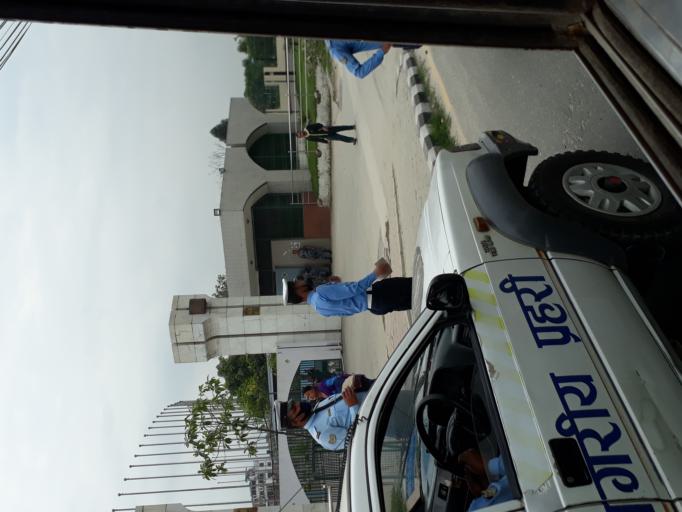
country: NP
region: Central Region
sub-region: Bagmati Zone
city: Kathmandu
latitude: 27.6881
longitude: 85.3369
